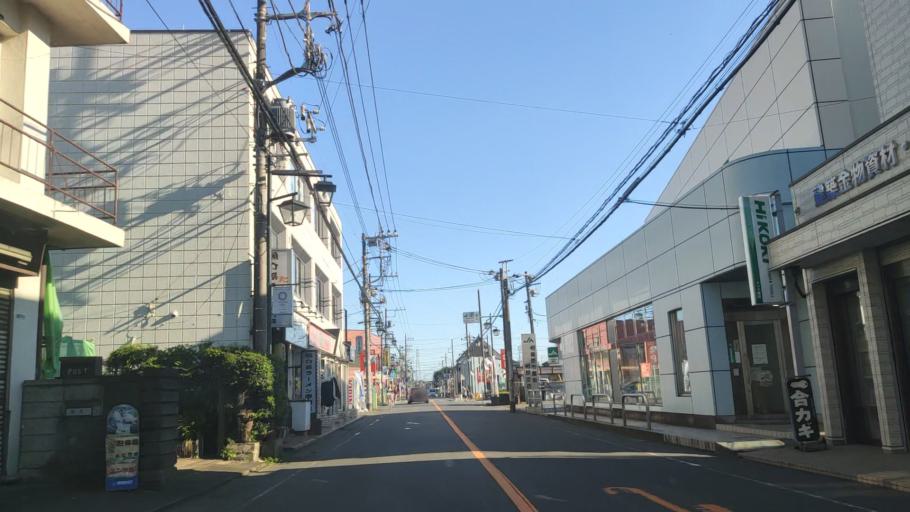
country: JP
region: Tokyo
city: Hachioji
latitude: 35.5967
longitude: 139.3207
